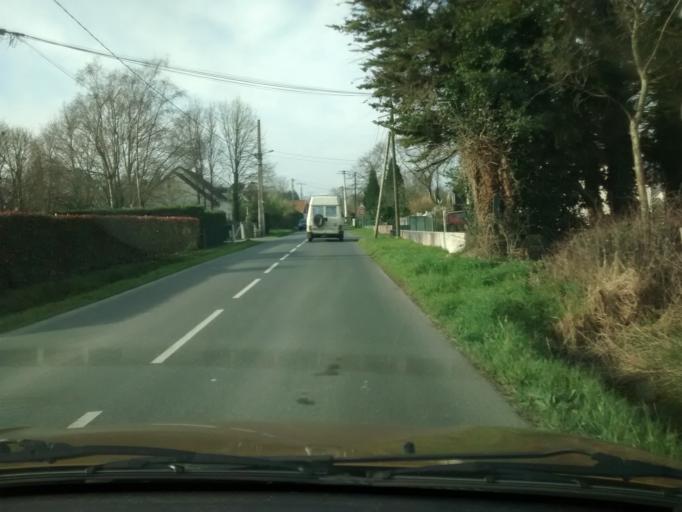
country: FR
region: Pays de la Loire
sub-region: Departement de la Loire-Atlantique
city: Notre-Dame-des-Landes
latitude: 47.3845
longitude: -1.7058
